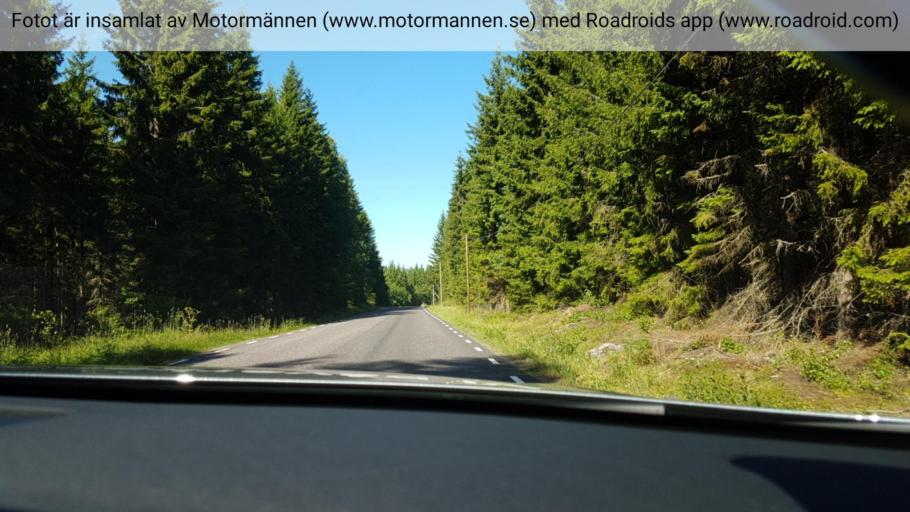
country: SE
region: Vaestra Goetaland
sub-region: Ulricehamns Kommun
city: Ulricehamn
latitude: 57.8384
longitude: 13.3415
